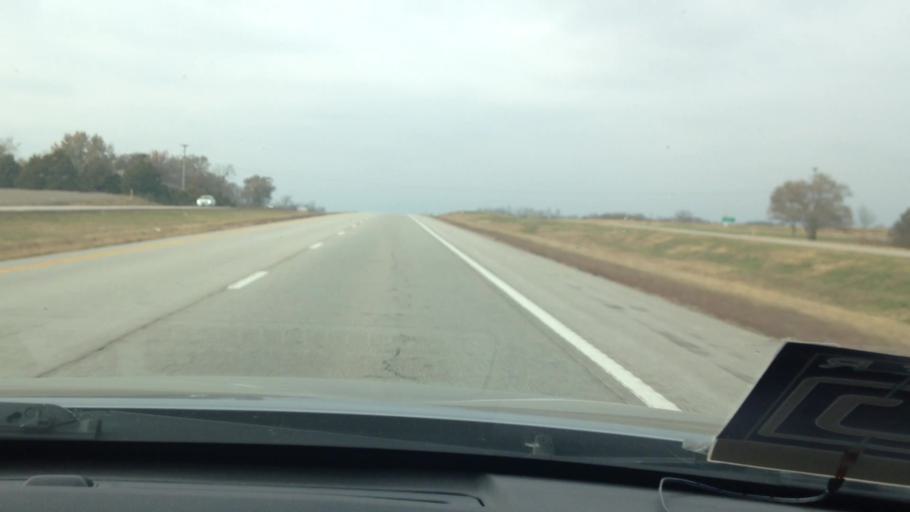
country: US
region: Missouri
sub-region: Cass County
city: Garden City
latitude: 38.5606
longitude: -94.1823
